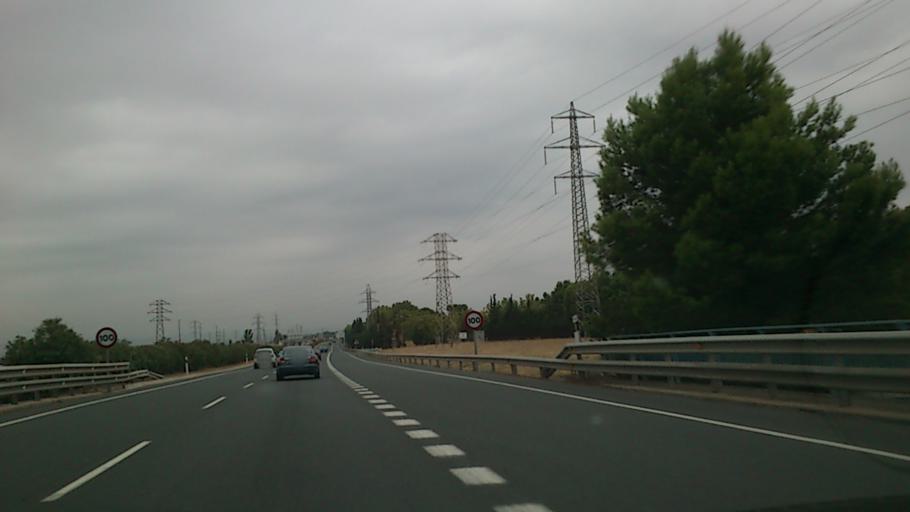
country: ES
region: Aragon
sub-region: Provincia de Zaragoza
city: Villanueva de Gallego
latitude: 41.7166
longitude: -0.8579
